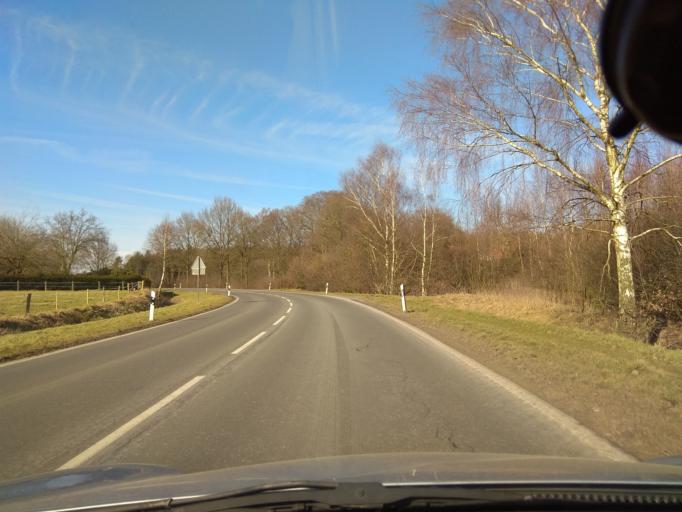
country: DE
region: North Rhine-Westphalia
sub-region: Regierungsbezirk Munster
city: Mettingen
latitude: 52.2805
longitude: 7.7843
